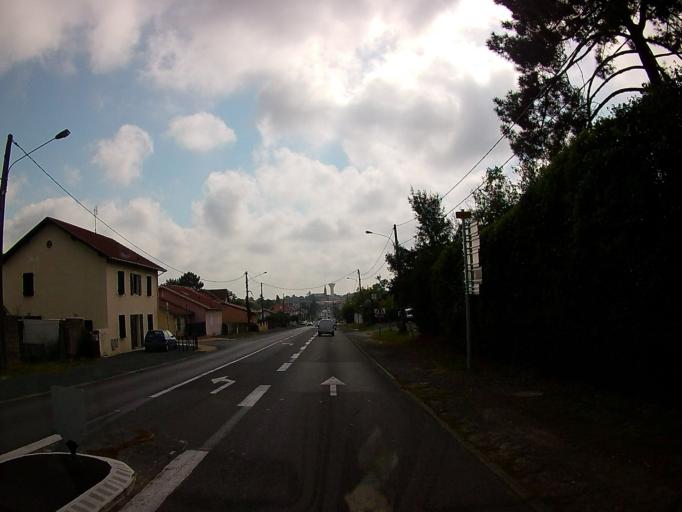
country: FR
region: Aquitaine
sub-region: Departement des Landes
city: Ondres
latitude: 43.5683
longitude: -1.4427
